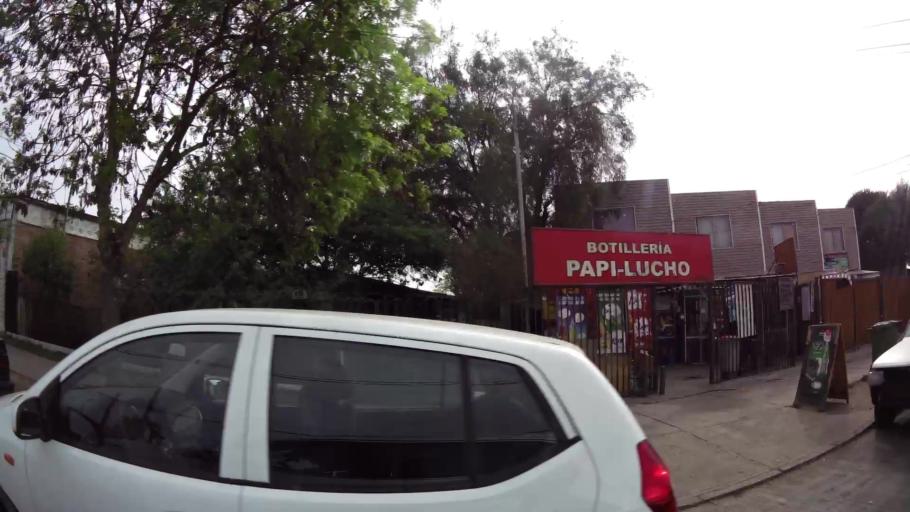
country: CL
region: Santiago Metropolitan
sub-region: Provincia de Santiago
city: Lo Prado
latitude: -33.5147
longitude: -70.7514
